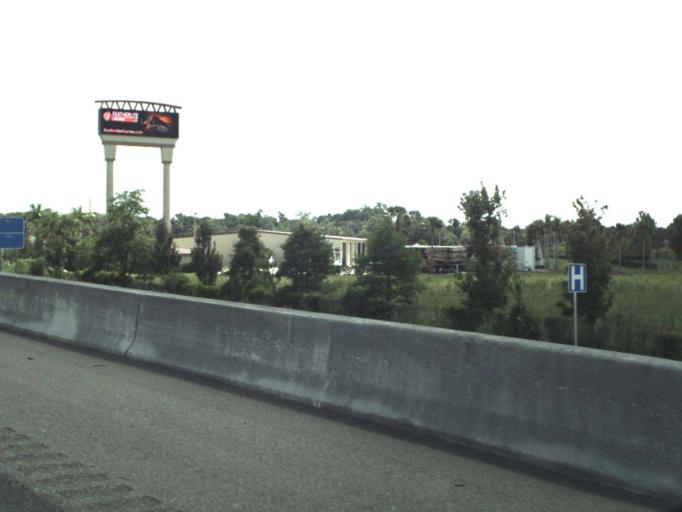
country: US
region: Florida
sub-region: Volusia County
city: DeBary
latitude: 28.8277
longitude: -81.3268
